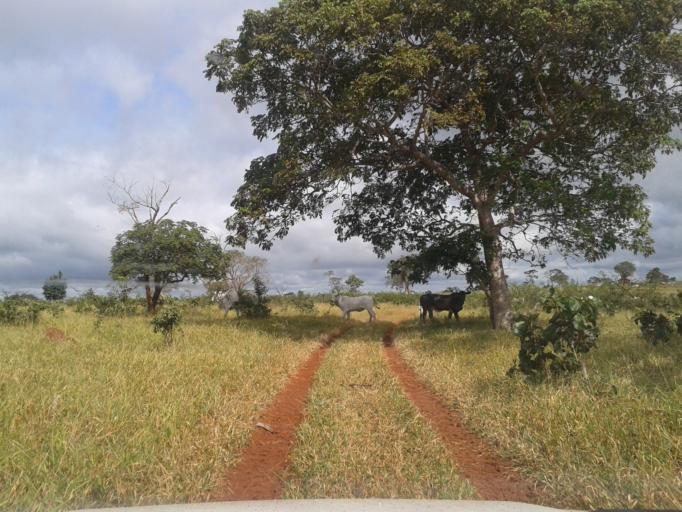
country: BR
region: Minas Gerais
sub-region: Campina Verde
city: Campina Verde
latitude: -19.4142
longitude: -49.6748
